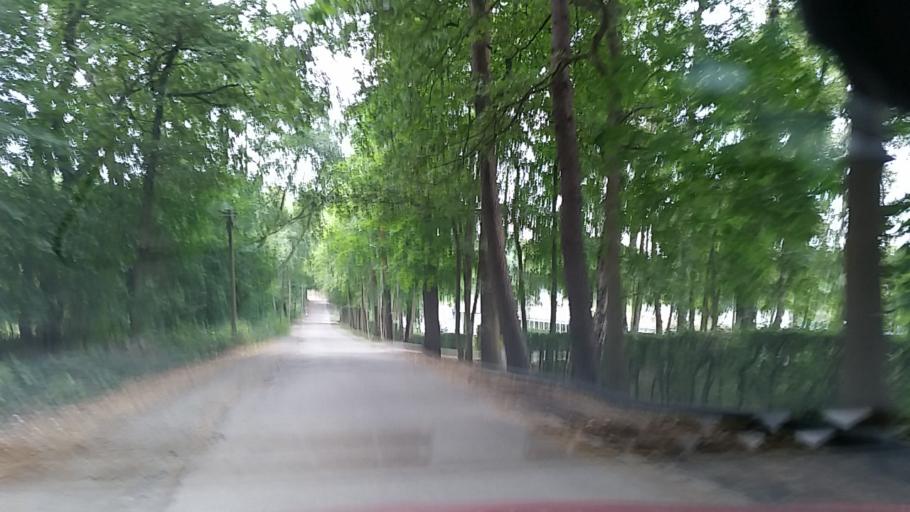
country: DE
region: Schleswig-Holstein
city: Wedel
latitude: 53.5730
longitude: 9.7750
